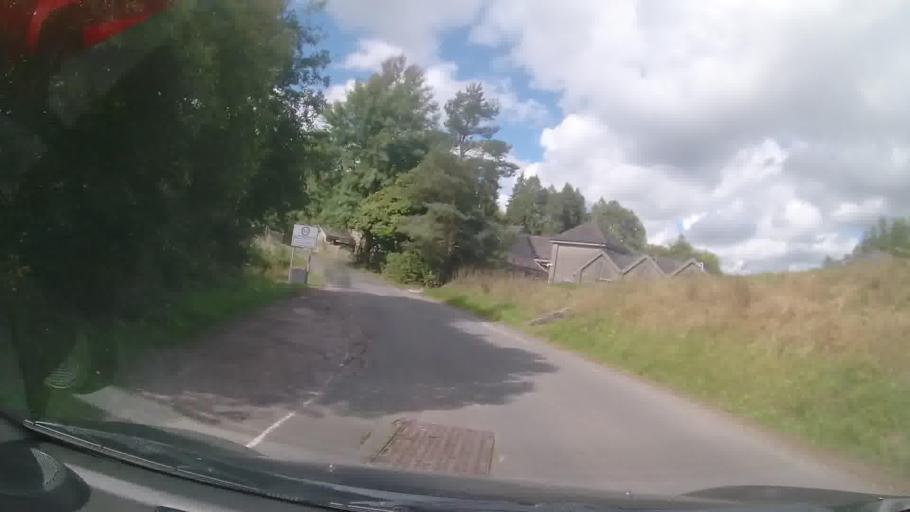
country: GB
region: Wales
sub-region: Merthyr Tydfil County Borough
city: Merthyr Tydfil
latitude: 51.7934
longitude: -3.3644
